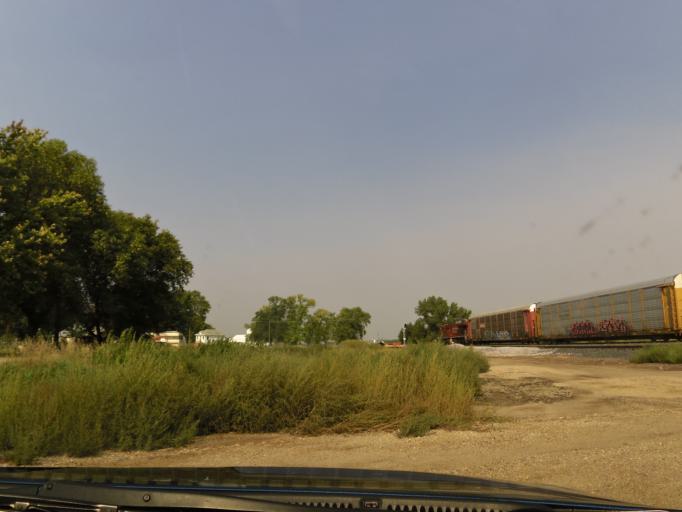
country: US
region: North Dakota
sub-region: Ransom County
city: Sheldon
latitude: 46.2657
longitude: -97.1274
